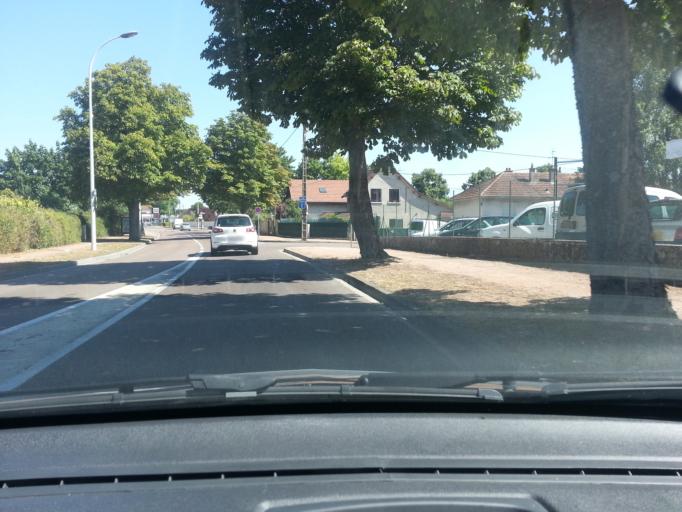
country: FR
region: Bourgogne
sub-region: Departement de la Cote-d'Or
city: Longvic
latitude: 47.3027
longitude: 5.0656
